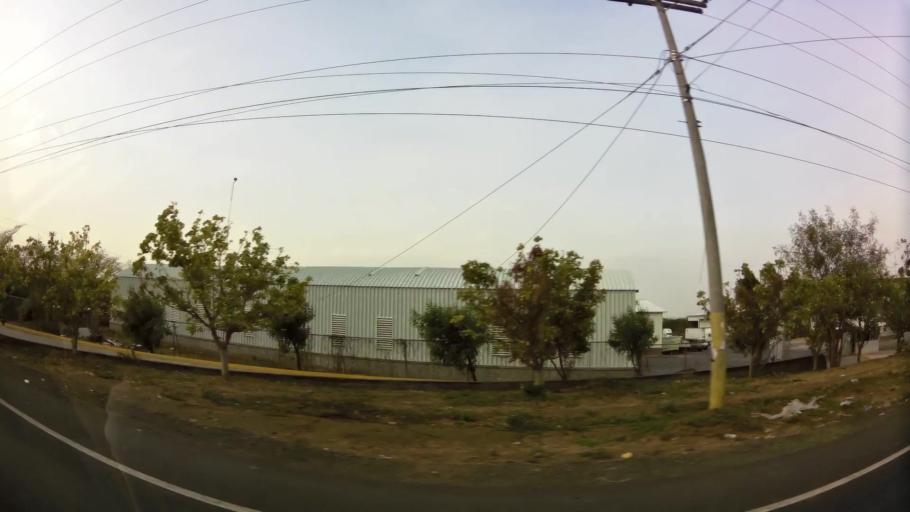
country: NI
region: Managua
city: Ciudad Sandino
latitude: 12.1776
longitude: -86.3518
